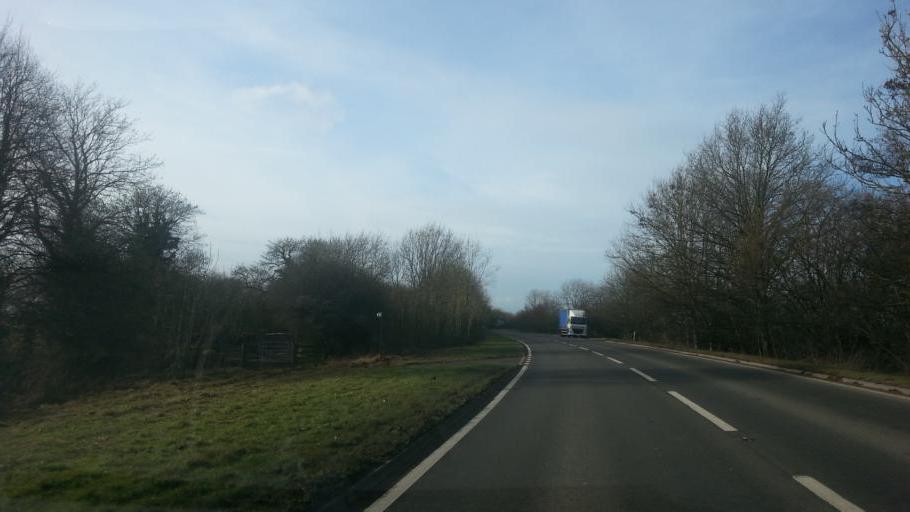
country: GB
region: England
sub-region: Leicestershire
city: Houghton on the Hill
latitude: 52.6187
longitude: -0.9119
